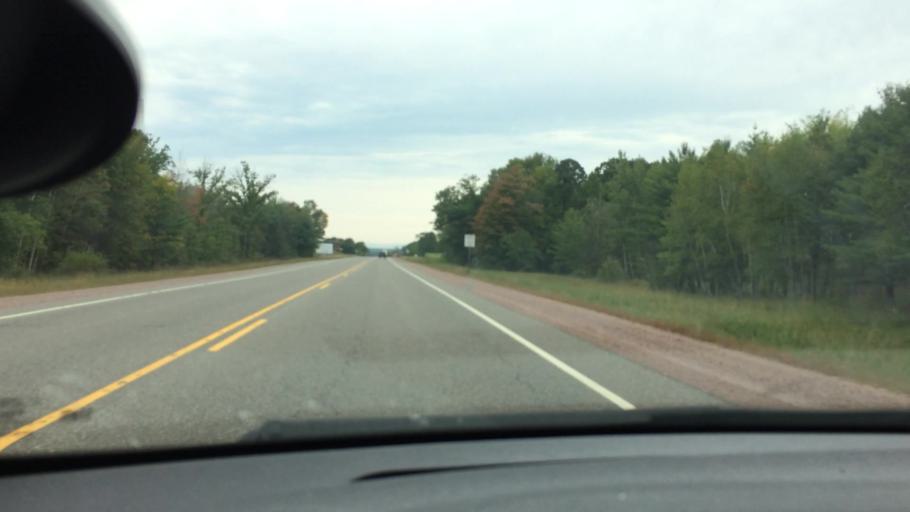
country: US
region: Wisconsin
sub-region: Clark County
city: Neillsville
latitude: 44.5628
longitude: -90.6528
